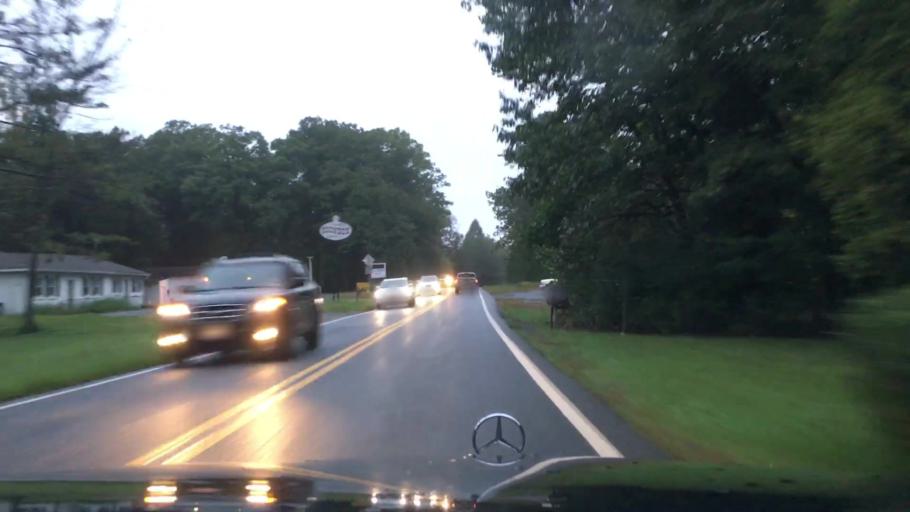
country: US
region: Virginia
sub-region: Campbell County
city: Timberlake
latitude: 37.2375
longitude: -79.2810
